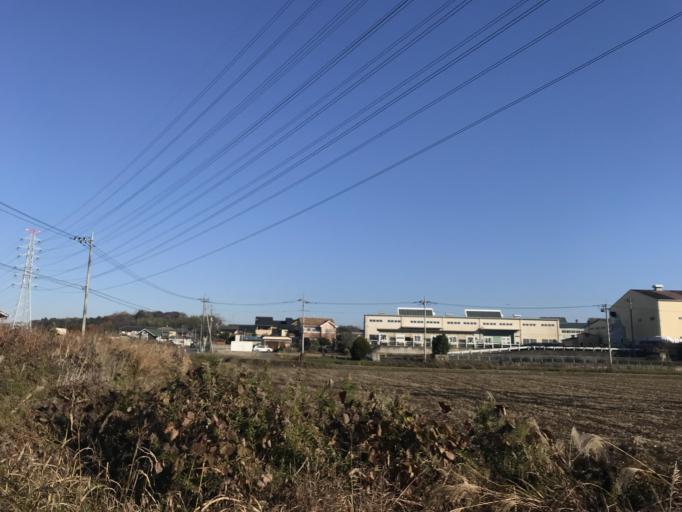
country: JP
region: Tochigi
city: Oyama
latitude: 36.2062
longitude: 139.8215
